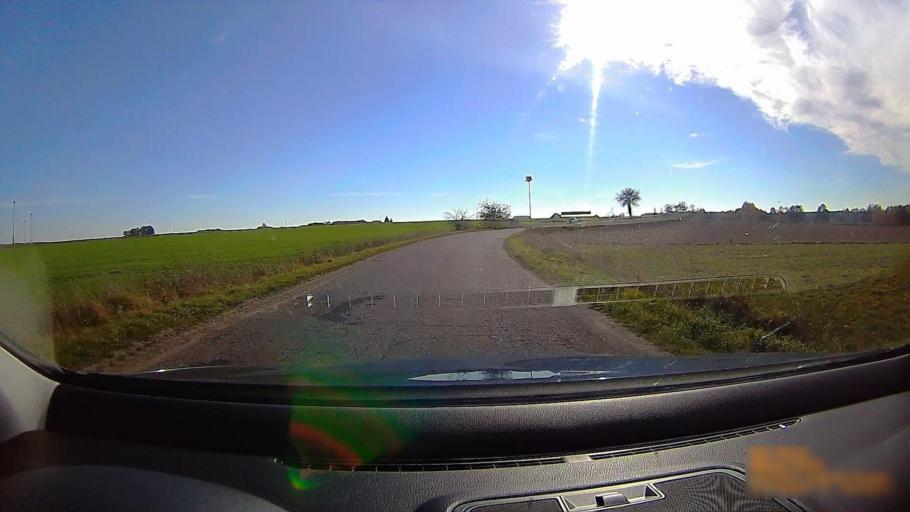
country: PL
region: Greater Poland Voivodeship
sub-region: Powiat ostrzeszowski
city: Doruchow
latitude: 51.3994
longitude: 18.0299
